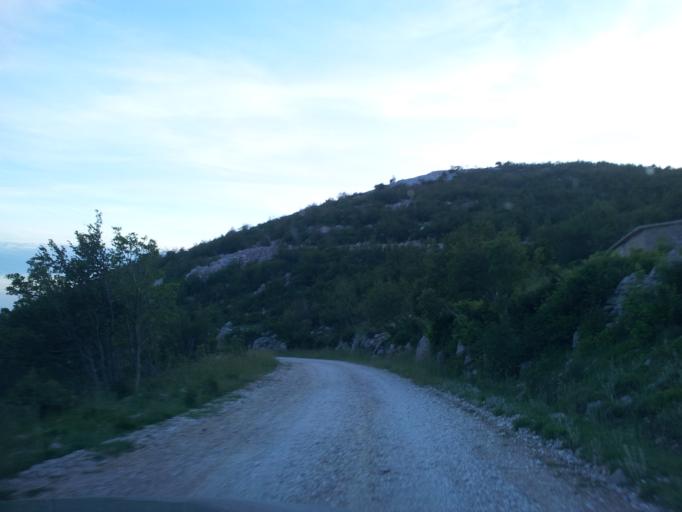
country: HR
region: Zadarska
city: Obrovac
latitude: 44.2577
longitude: 15.6413
